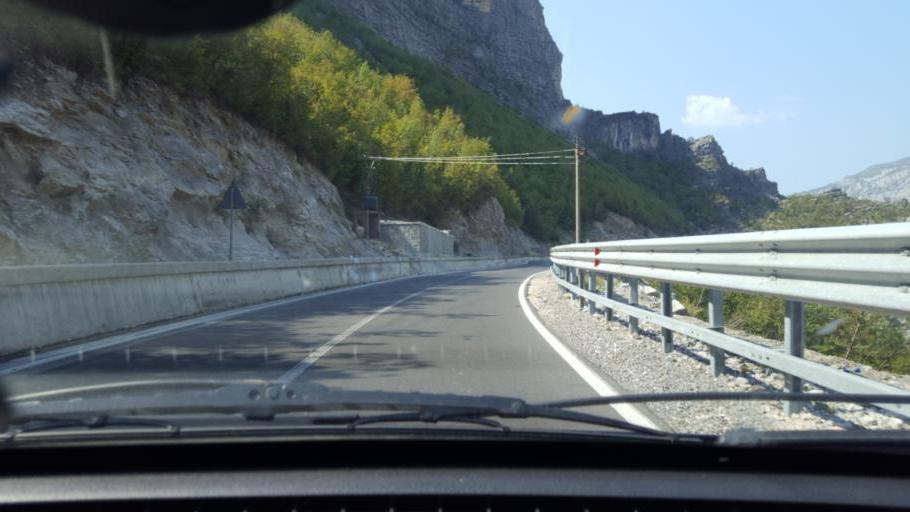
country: AL
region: Shkoder
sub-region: Rrethi i Malesia e Madhe
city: Kastrat
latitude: 42.4152
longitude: 19.5082
